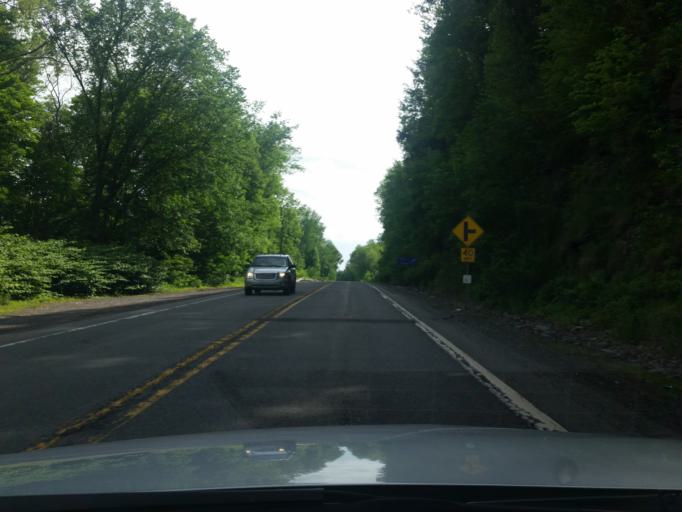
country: US
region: Pennsylvania
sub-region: Luzerne County
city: Back Mountain
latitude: 41.3074
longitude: -76.0388
